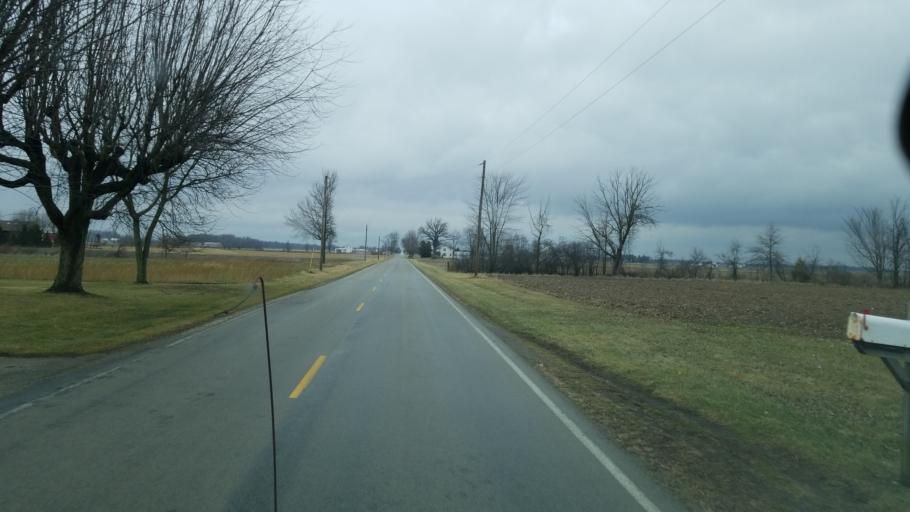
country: US
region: Ohio
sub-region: Hardin County
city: Forest
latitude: 40.7911
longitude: -83.4194
